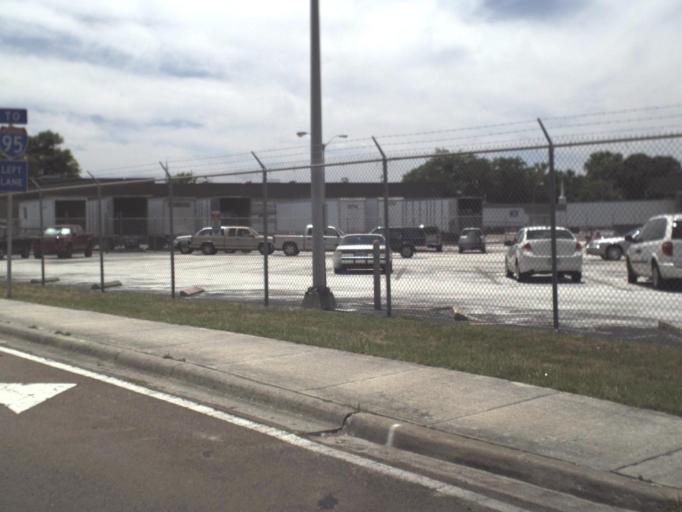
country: US
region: Florida
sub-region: Duval County
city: Jacksonville
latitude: 30.3368
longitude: -81.6701
